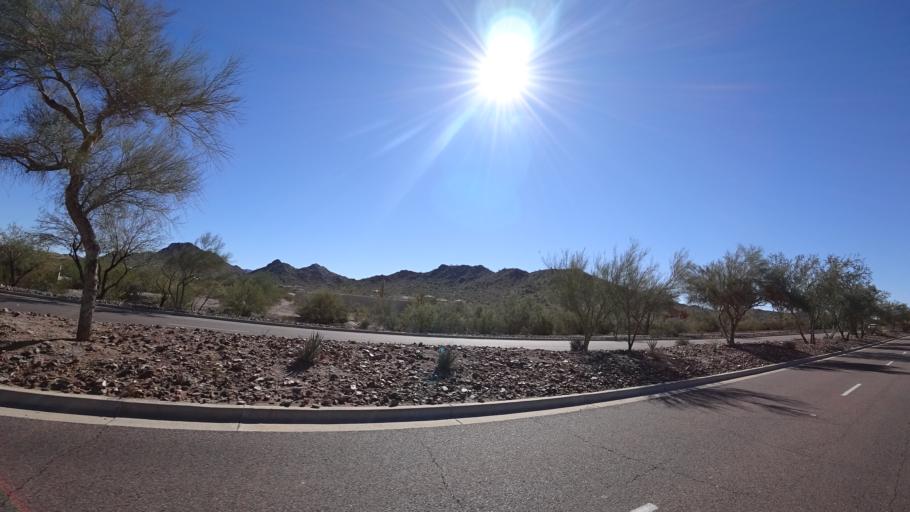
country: US
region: Arizona
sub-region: Maricopa County
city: Goodyear
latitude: 33.3631
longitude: -112.4078
